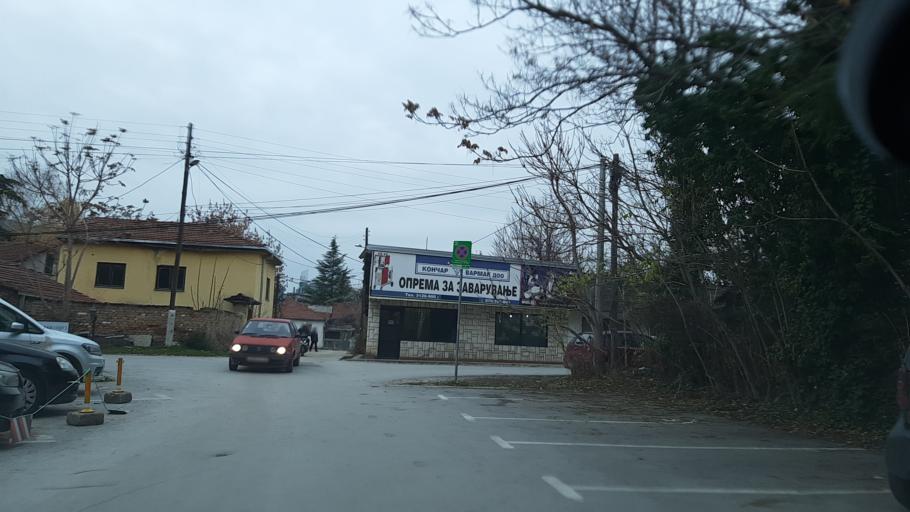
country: MK
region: Karpos
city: Skopje
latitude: 41.9911
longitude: 21.4411
